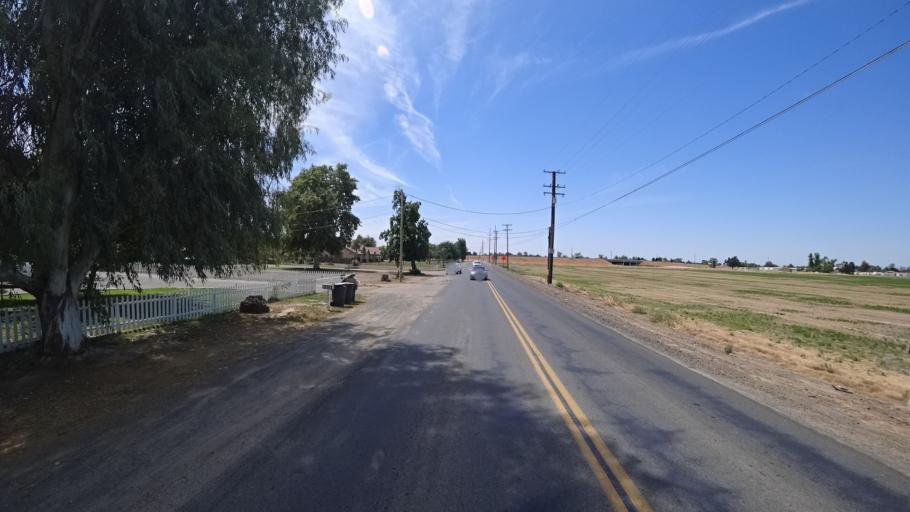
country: US
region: California
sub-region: Kings County
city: Armona
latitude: 36.3177
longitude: -119.6910
